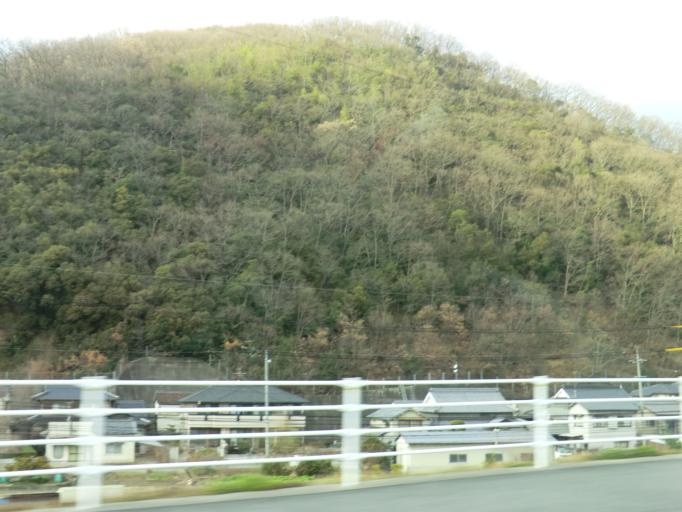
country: JP
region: Okayama
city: Okayama-shi
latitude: 34.7065
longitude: 133.9467
